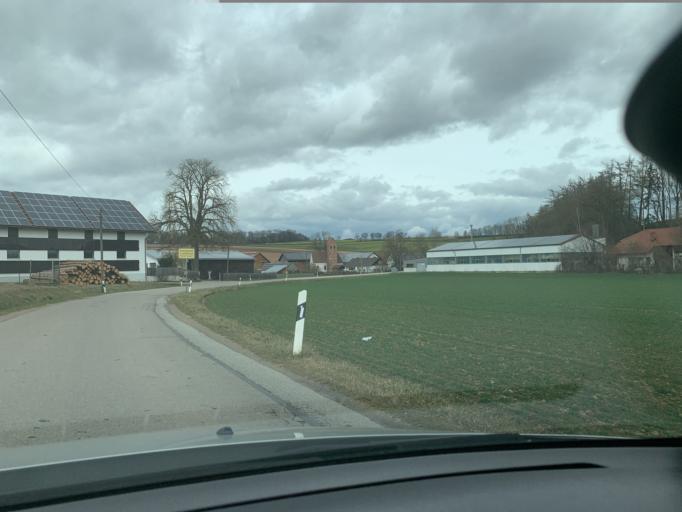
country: DE
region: Bavaria
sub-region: Lower Bavaria
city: Landshut
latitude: 48.5171
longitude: 12.1758
